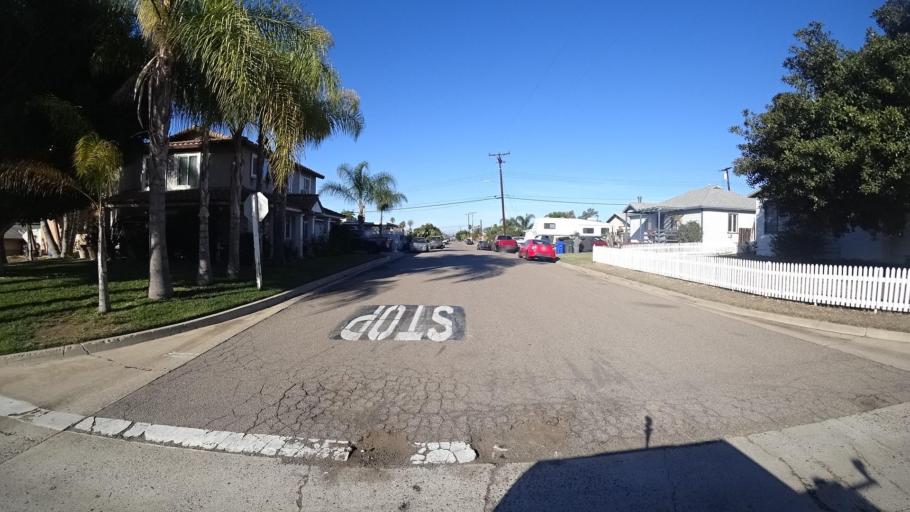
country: US
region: California
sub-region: San Diego County
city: La Presa
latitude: 32.7135
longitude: -116.9949
